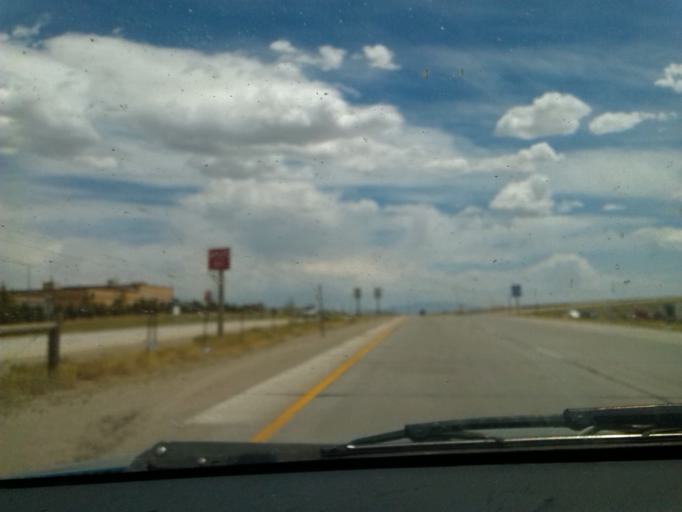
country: US
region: Wyoming
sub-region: Carbon County
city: Rawlins
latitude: 41.7916
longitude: -107.2069
